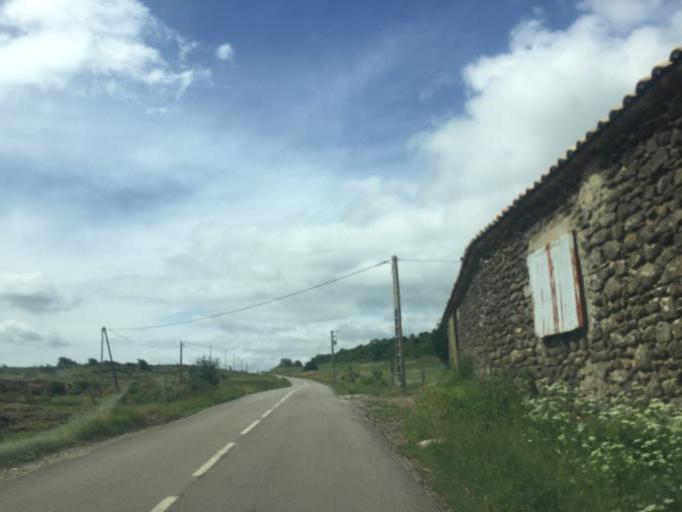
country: FR
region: Rhone-Alpes
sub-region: Departement de l'Ardeche
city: Saint-Priest
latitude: 44.6707
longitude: 4.5605
